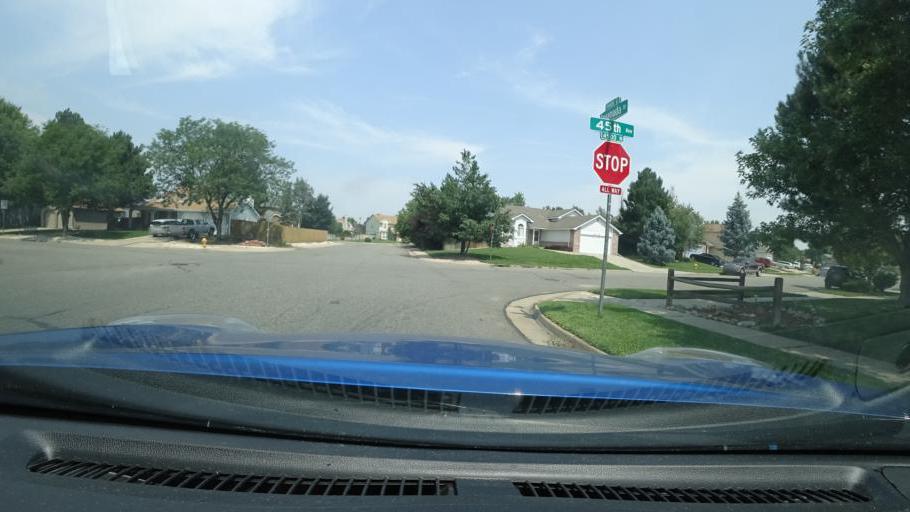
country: US
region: Colorado
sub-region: Adams County
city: Aurora
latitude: 39.7763
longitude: -104.7604
